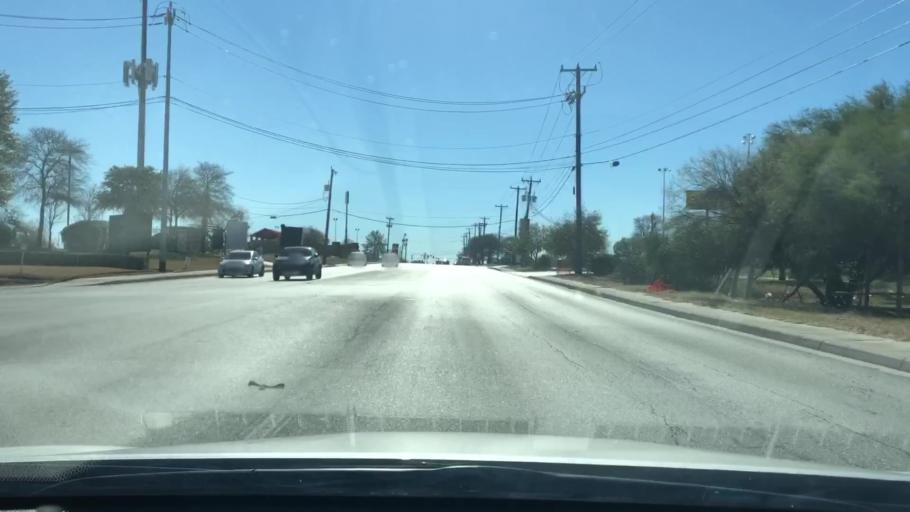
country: US
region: Texas
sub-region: Bexar County
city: Kirby
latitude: 29.4494
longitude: -98.3608
